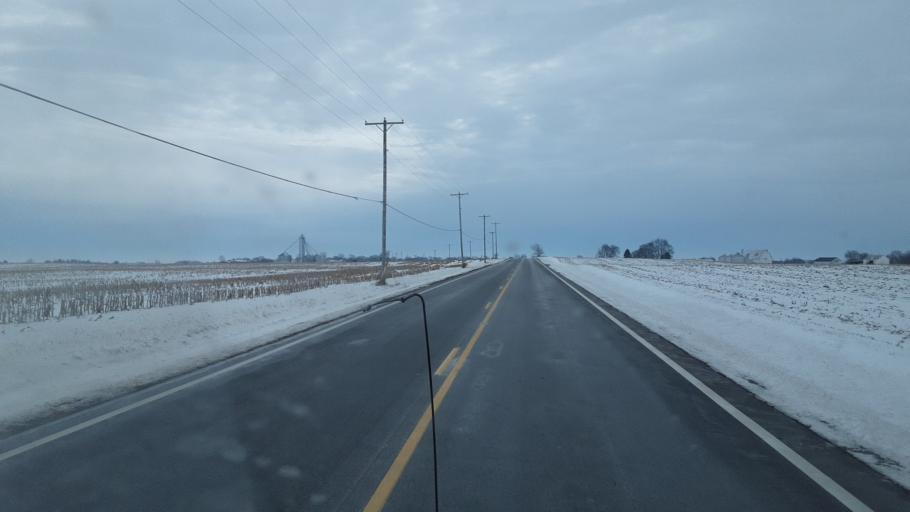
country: US
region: Ohio
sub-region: Madison County
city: Bethel
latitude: 39.7500
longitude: -83.4813
